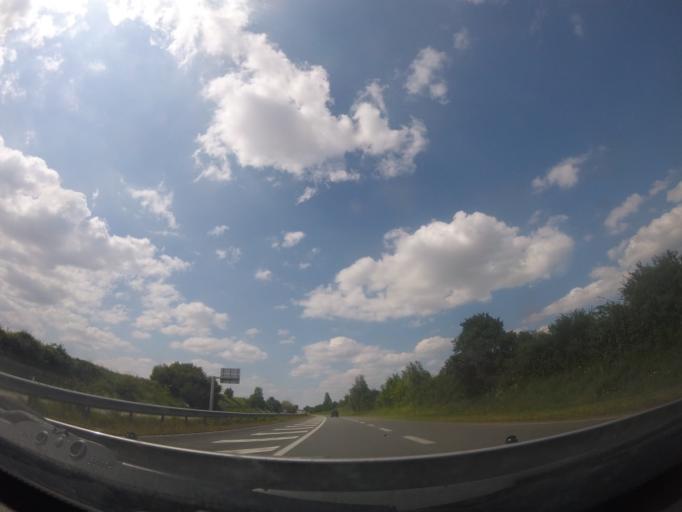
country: FR
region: Poitou-Charentes
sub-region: Departement de la Charente-Maritime
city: Saint-Porchaire
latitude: 45.8290
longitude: -0.7972
